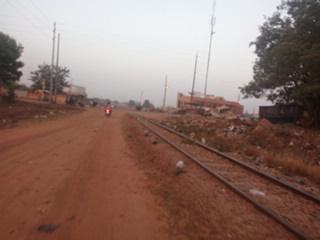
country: BJ
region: Borgou
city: Parakou
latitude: 9.3403
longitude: 2.6059
